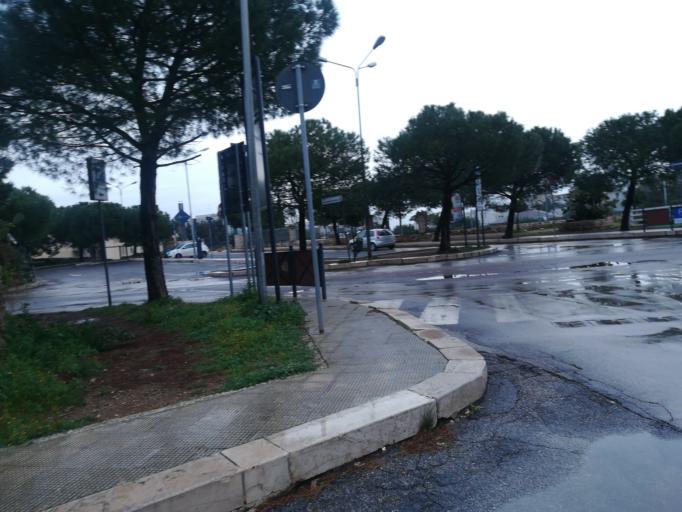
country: IT
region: Apulia
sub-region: Provincia di Bari
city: Polignano a Mare
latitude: 40.9941
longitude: 17.2157
